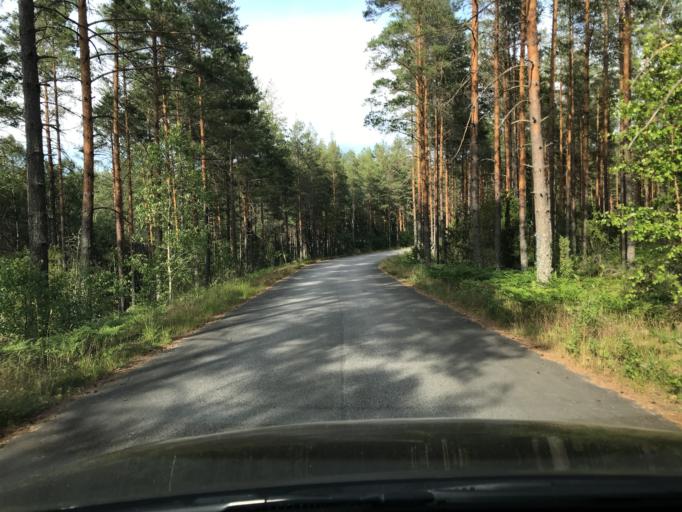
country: SE
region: Kalmar
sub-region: Hultsfreds Kommun
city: Malilla
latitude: 57.3953
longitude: 15.8054
